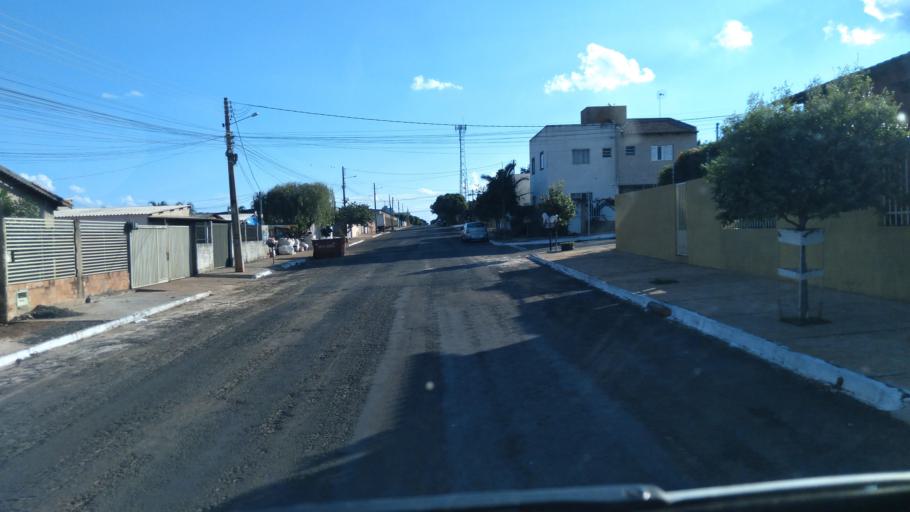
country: BR
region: Goias
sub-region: Mineiros
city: Mineiros
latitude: -17.5587
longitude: -52.5475
